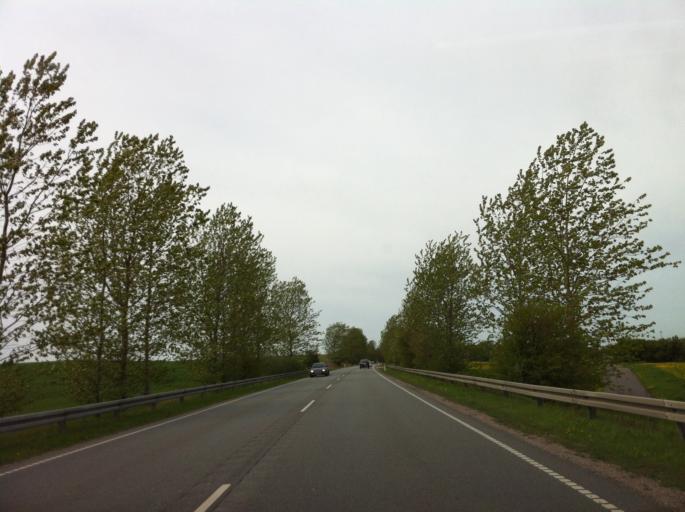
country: DK
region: Capital Region
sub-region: Hillerod Kommune
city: Hillerod
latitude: 55.9062
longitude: 12.2984
